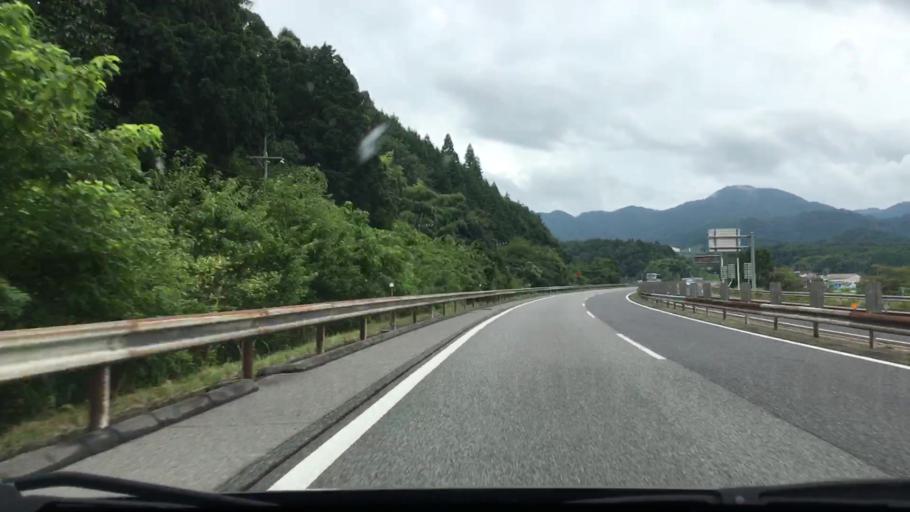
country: JP
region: Hiroshima
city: Hiroshima-shi
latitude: 34.6703
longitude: 132.5405
